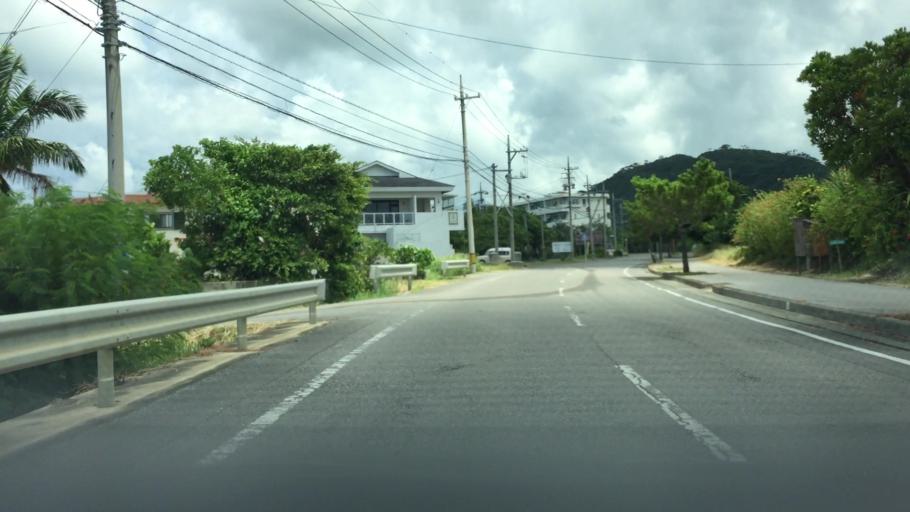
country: JP
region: Okinawa
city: Ishigaki
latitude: 24.3606
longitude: 124.1437
